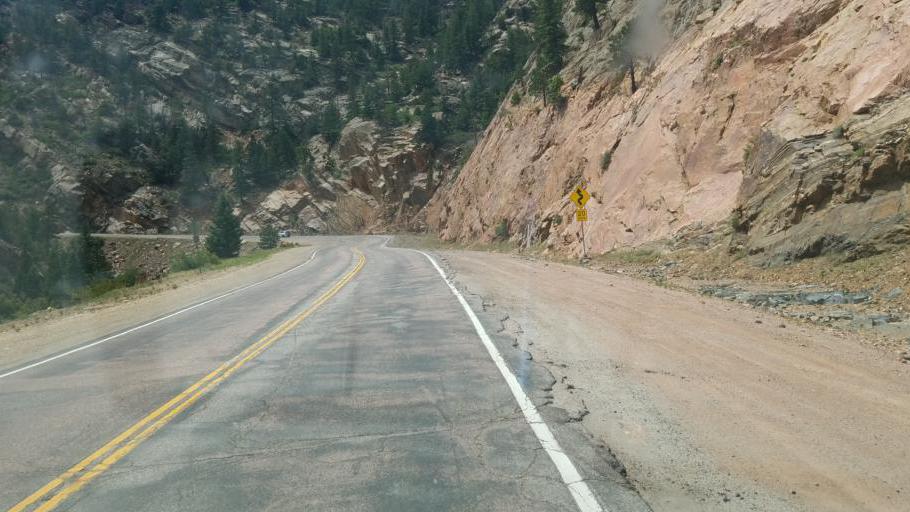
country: US
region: Colorado
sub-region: Fremont County
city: Florence
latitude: 38.1745
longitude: -105.1705
